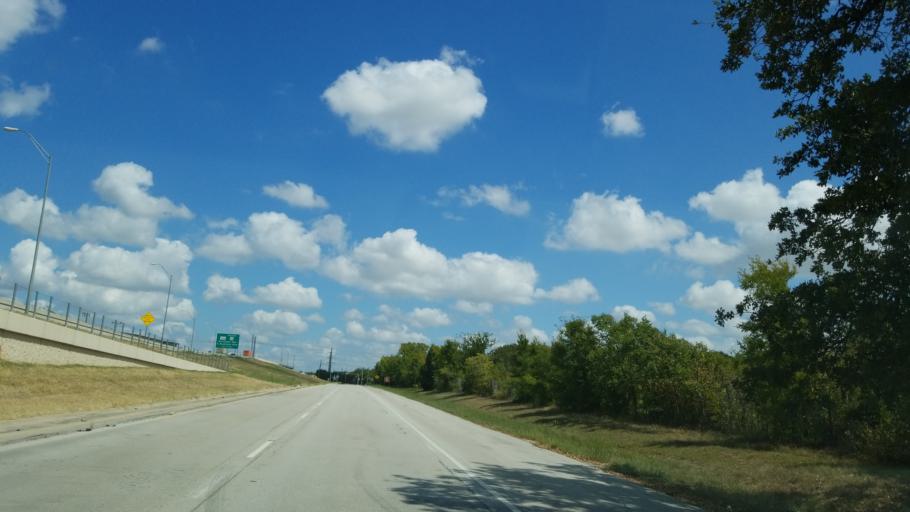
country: US
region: Texas
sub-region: Tarrant County
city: Grapevine
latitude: 32.9171
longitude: -97.0924
